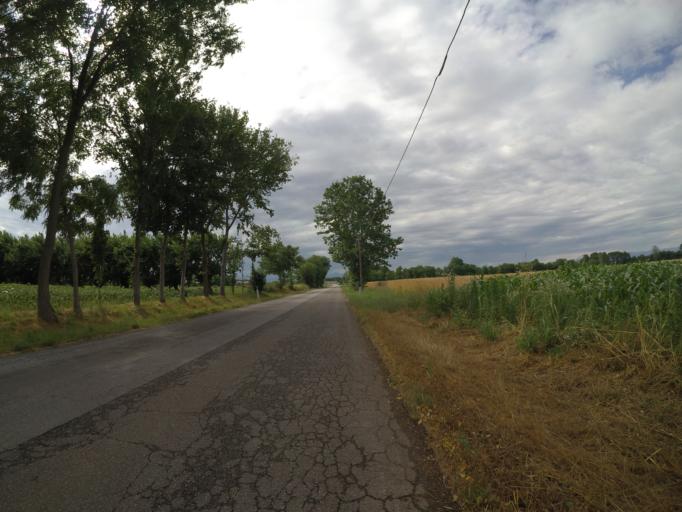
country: IT
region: Friuli Venezia Giulia
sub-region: Provincia di Udine
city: Lestizza
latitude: 45.9610
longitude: 13.1279
